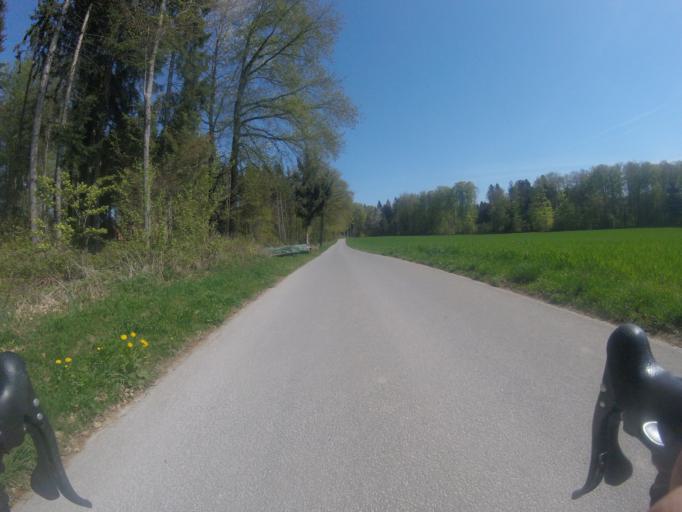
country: CH
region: Fribourg
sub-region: Sense District
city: Flamatt
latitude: 46.9110
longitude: 7.2868
